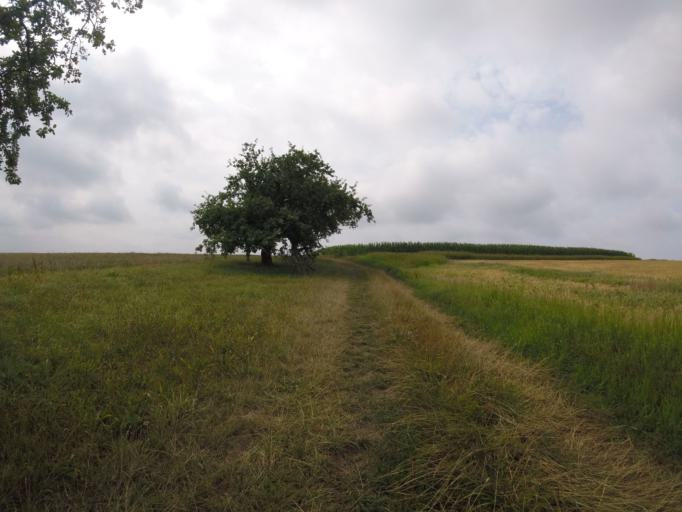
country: DE
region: Baden-Wuerttemberg
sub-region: Regierungsbezirk Stuttgart
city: Aspach
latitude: 48.9628
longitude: 9.3902
